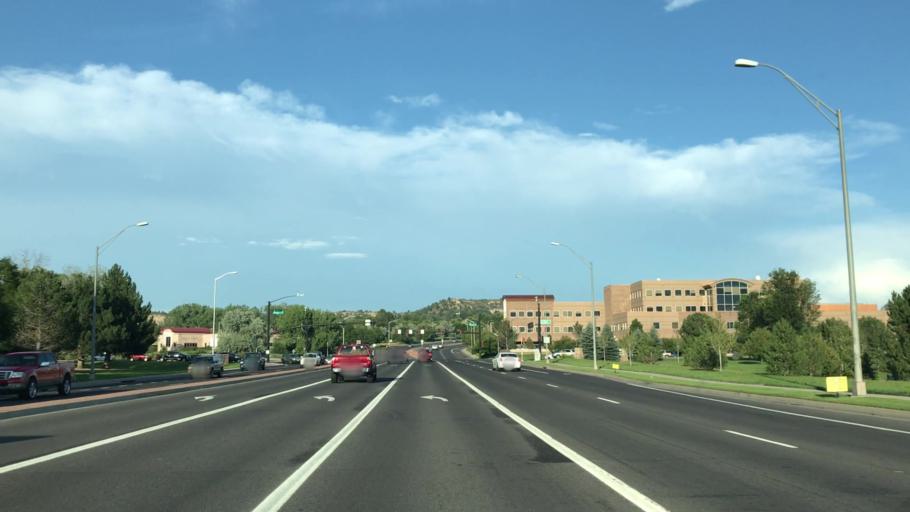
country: US
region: Colorado
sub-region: El Paso County
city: Colorado Springs
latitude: 38.8736
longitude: -104.7970
